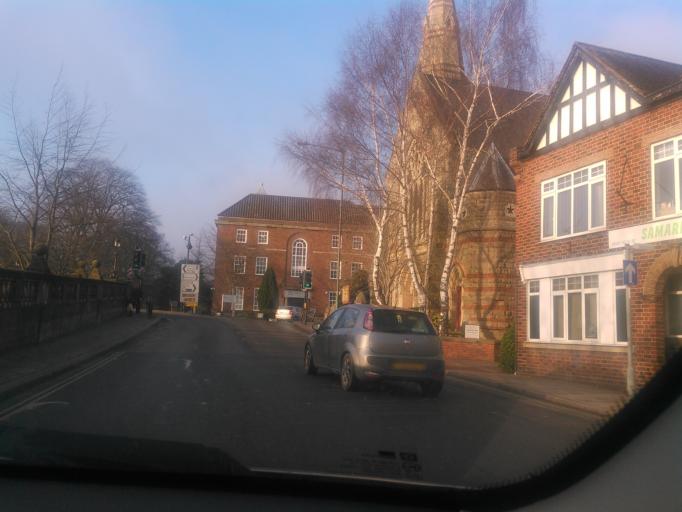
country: GB
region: England
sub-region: Shropshire
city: Shrewsbury
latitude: 52.7064
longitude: -2.7465
